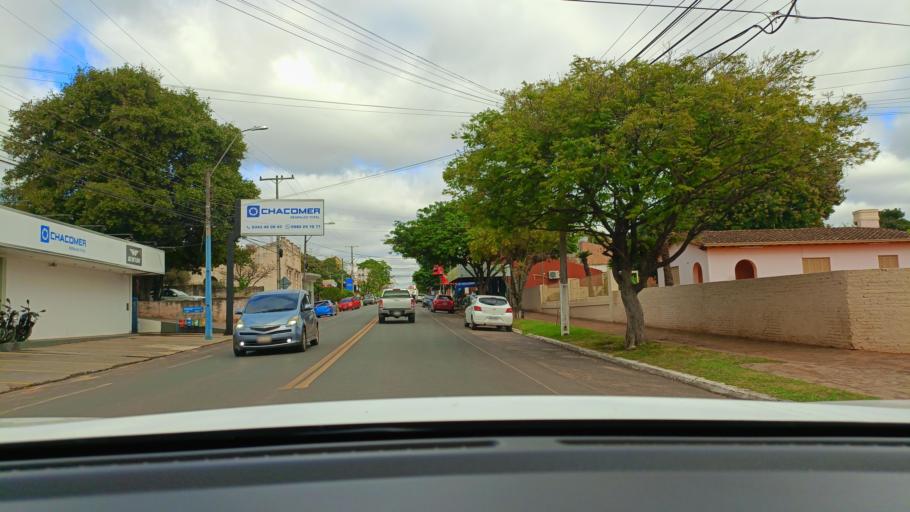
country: PY
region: San Pedro
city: Guayaybi
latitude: -24.6673
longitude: -56.4447
